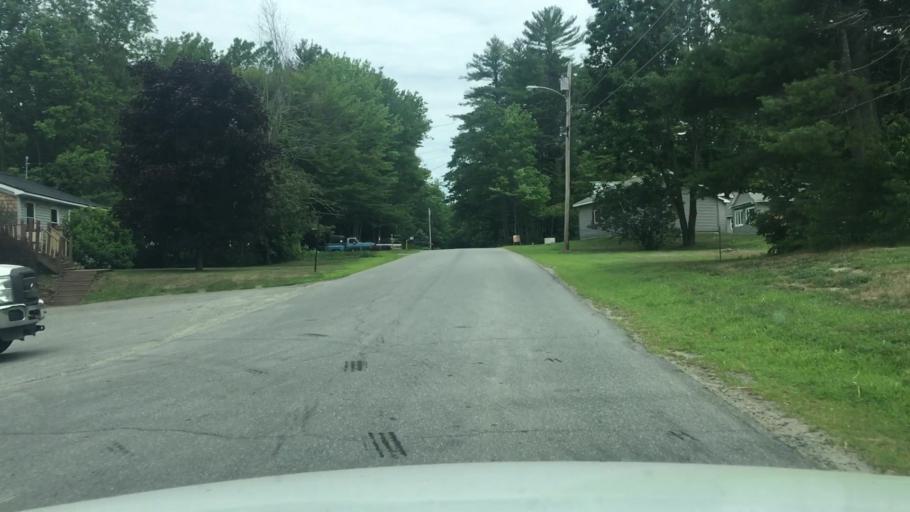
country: US
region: Maine
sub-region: Kennebec County
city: Albion
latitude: 44.5858
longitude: -69.4710
